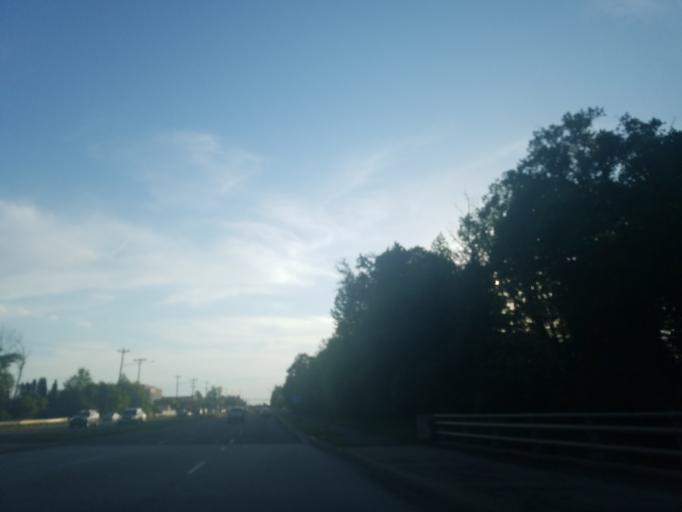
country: US
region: Virginia
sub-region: Fairfax County
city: Centreville
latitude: 38.8367
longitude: -77.4494
